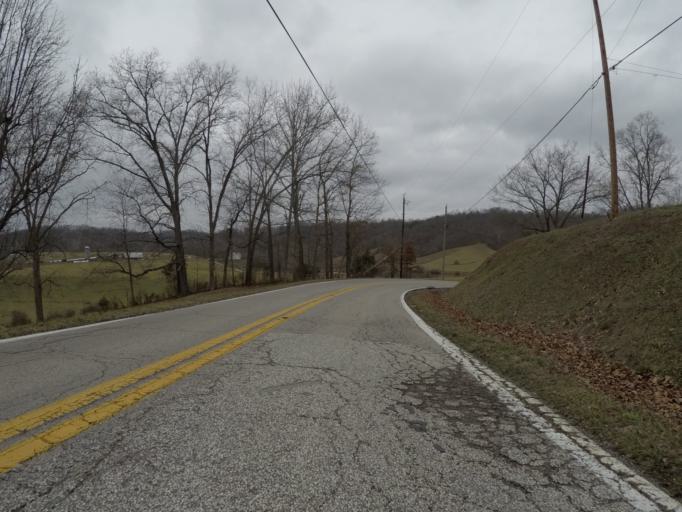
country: US
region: West Virginia
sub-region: Cabell County
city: Barboursville
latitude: 38.4331
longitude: -82.2440
